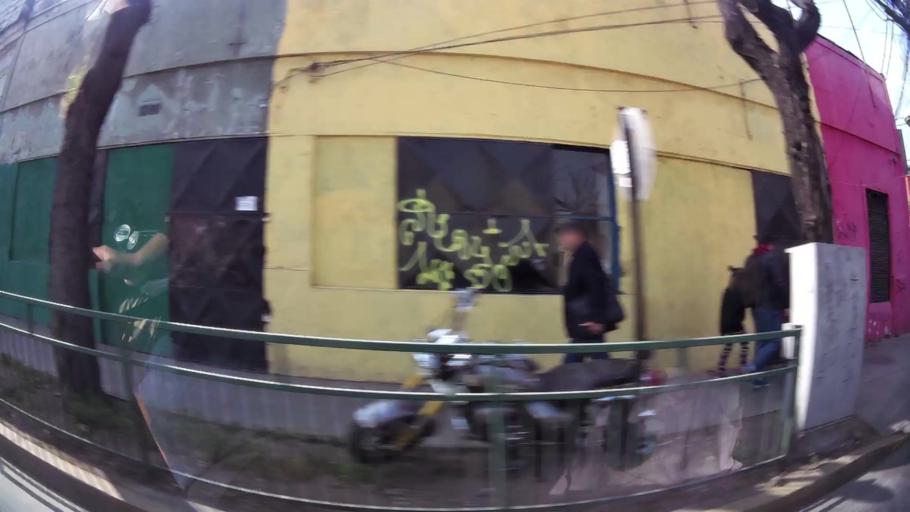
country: CL
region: Santiago Metropolitan
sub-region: Provincia de Santiago
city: Santiago
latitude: -33.4629
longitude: -70.6427
